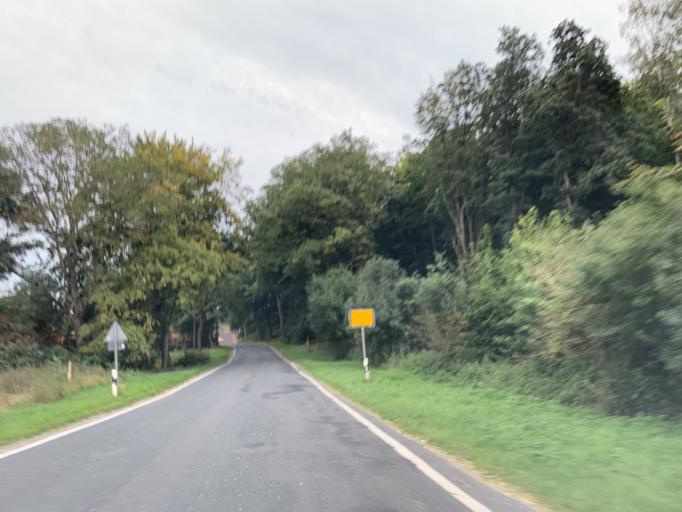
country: DE
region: Mecklenburg-Vorpommern
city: Woldegk
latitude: 53.3371
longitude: 13.6095
